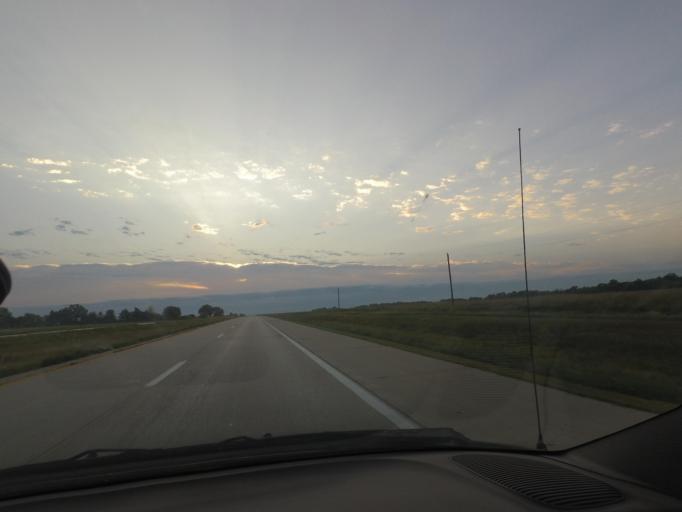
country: US
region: Missouri
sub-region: Macon County
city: Macon
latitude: 39.7502
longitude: -92.3540
